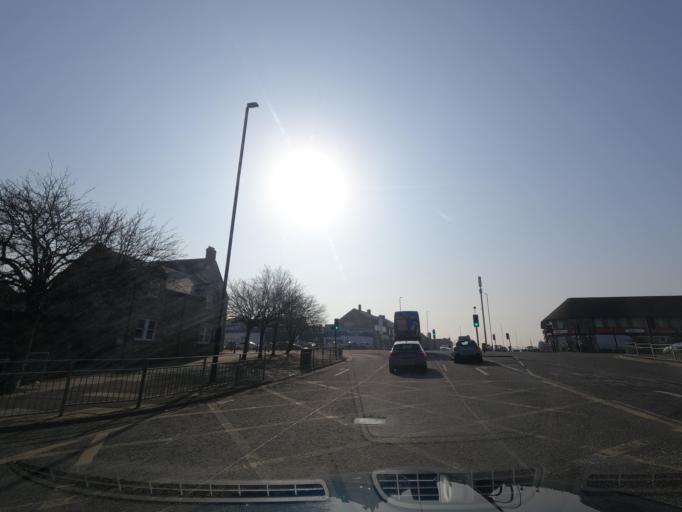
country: GB
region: England
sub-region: Newcastle upon Tyne
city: Gosforth
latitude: 55.0096
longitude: -1.5788
